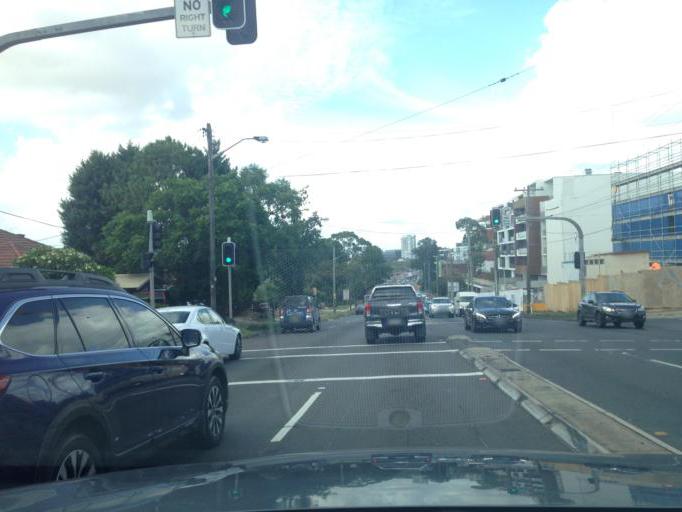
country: AU
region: New South Wales
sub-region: Canada Bay
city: Rhodes
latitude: -33.8191
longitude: 151.1002
